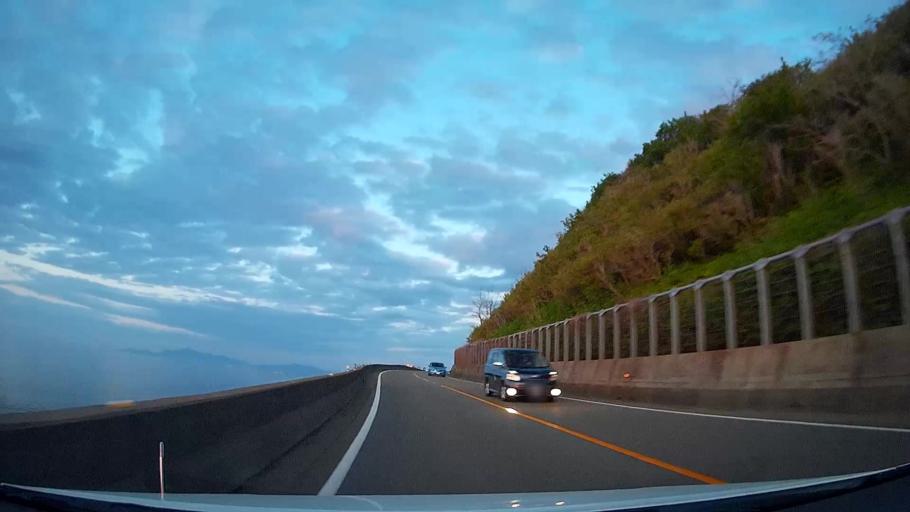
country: JP
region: Niigata
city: Joetsu
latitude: 37.1705
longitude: 138.1187
